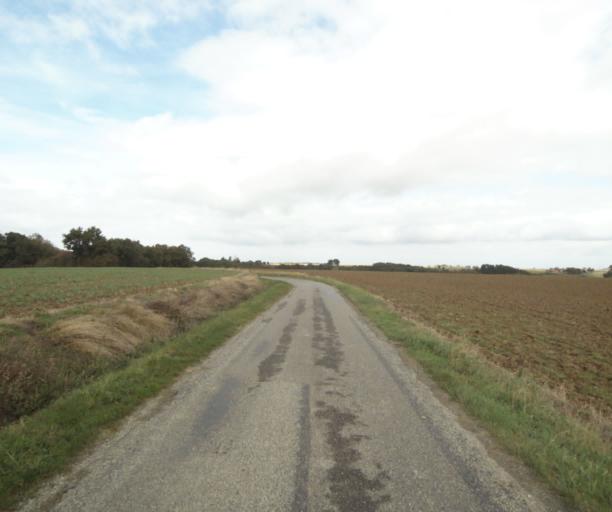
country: FR
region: Midi-Pyrenees
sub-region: Departement du Tarn-et-Garonne
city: Beaumont-de-Lomagne
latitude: 43.8732
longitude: 1.0889
